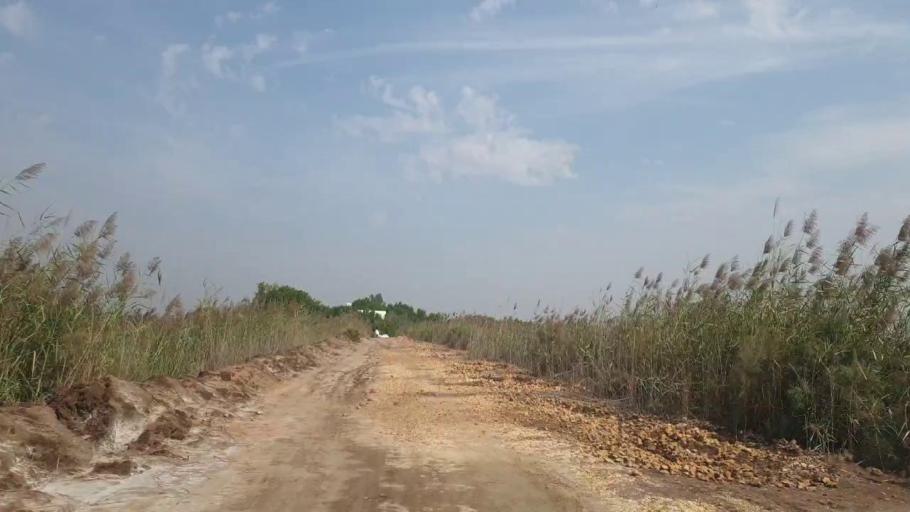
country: PK
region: Sindh
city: Rajo Khanani
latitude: 24.9985
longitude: 69.0028
